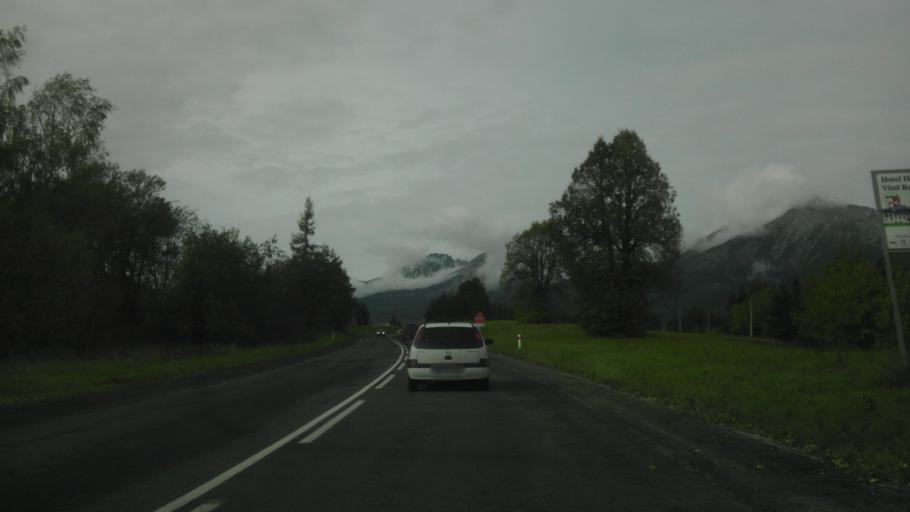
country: SK
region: Presovsky
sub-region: Okres Poprad
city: Nova Lesna
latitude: 49.1159
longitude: 20.2606
